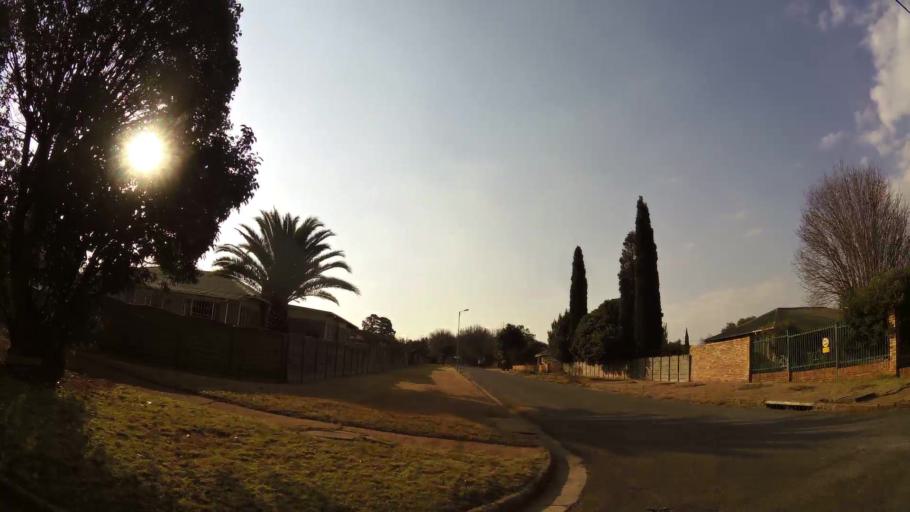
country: ZA
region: Gauteng
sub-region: Ekurhuleni Metropolitan Municipality
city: Springs
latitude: -26.2780
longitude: 28.4489
